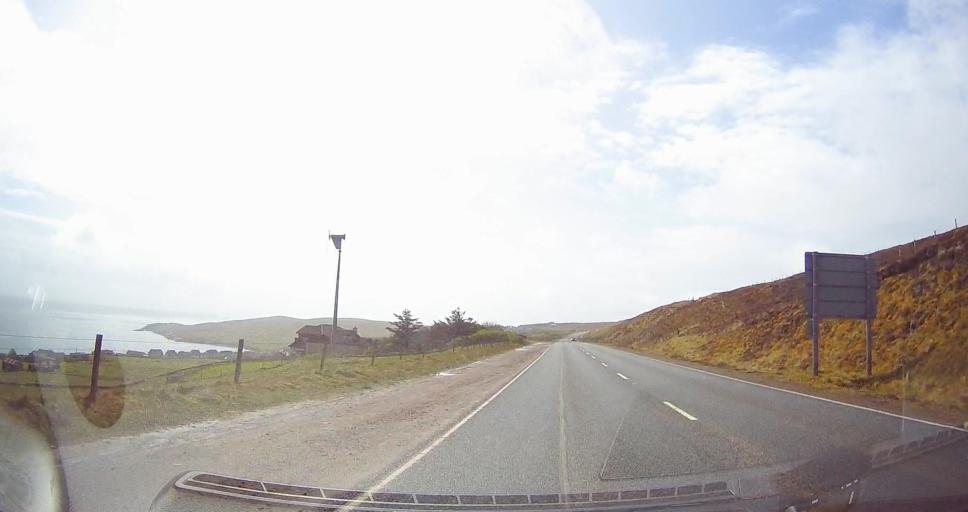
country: GB
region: Scotland
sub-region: Shetland Islands
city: Lerwick
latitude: 60.1346
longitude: -1.2141
